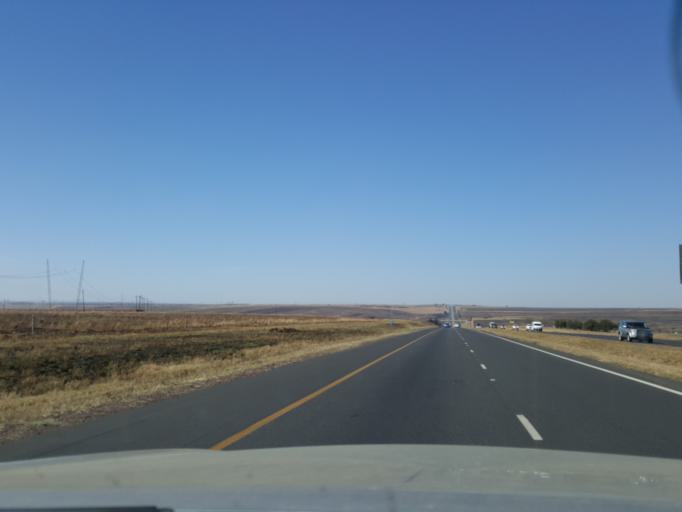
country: ZA
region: Mpumalanga
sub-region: Nkangala District Municipality
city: Middelburg
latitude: -25.8316
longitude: 29.4743
